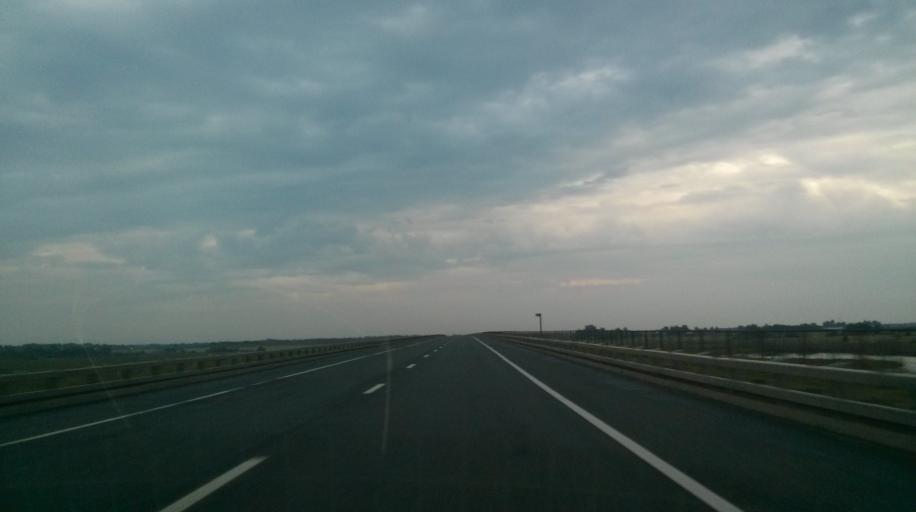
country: RU
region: Vladimir
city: Murom
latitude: 55.5920
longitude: 42.1164
